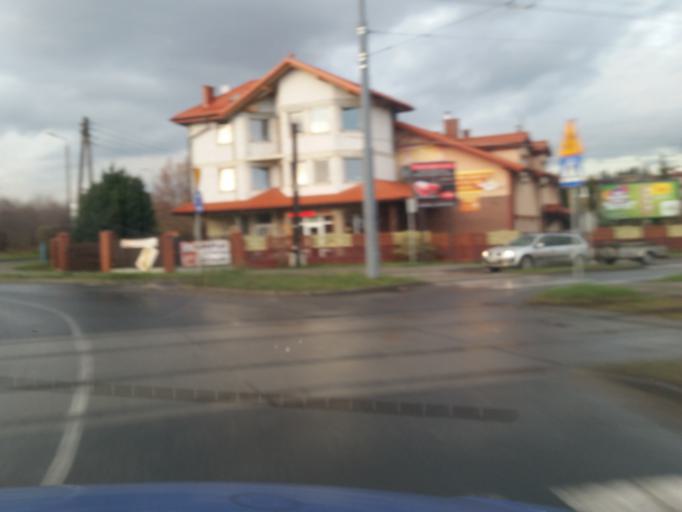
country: PL
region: Silesian Voivodeship
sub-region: Myslowice
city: Myslowice
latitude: 50.2724
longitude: 19.1776
